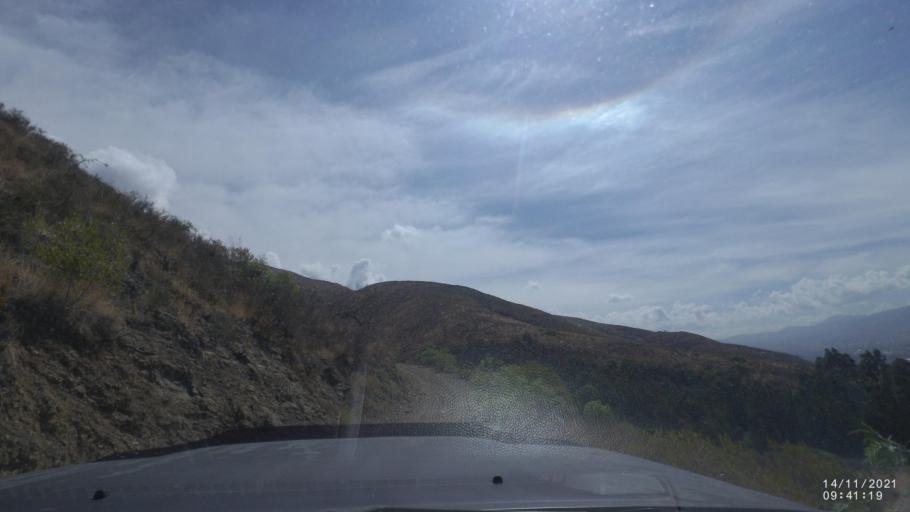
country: BO
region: Cochabamba
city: Cochabamba
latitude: -17.3639
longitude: -66.0855
